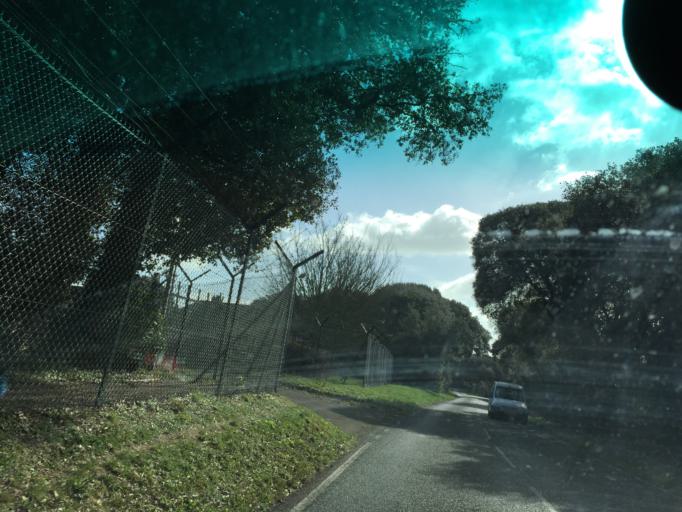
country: GB
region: England
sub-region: Hampshire
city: Gosport
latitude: 50.7792
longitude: -1.1413
